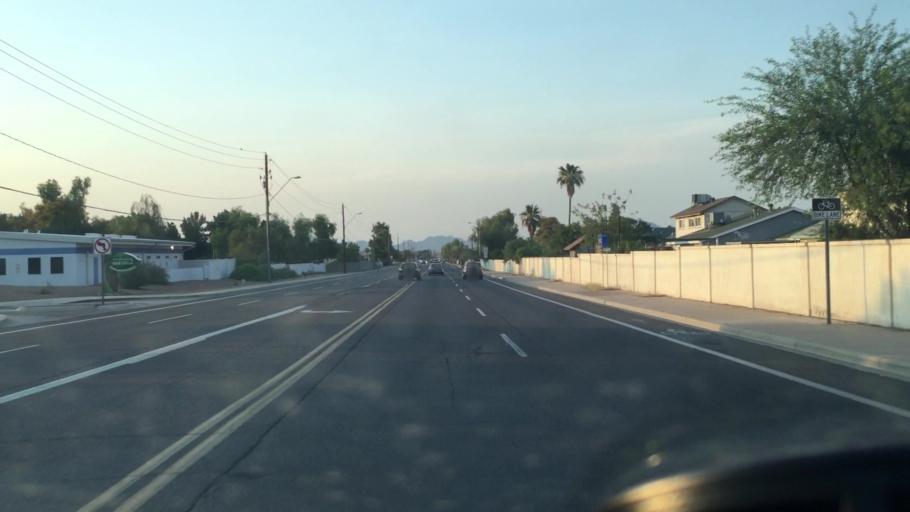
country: US
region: Arizona
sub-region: Maricopa County
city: Guadalupe
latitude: 33.3855
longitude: -111.9955
